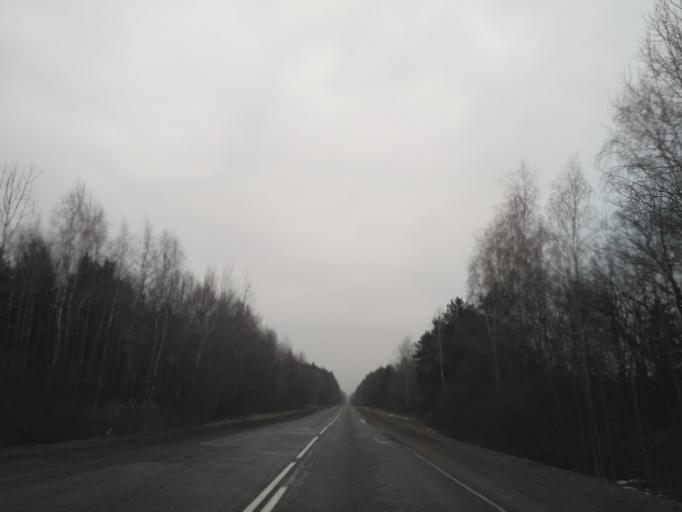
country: BY
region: Minsk
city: Snow
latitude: 53.2838
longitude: 26.3644
